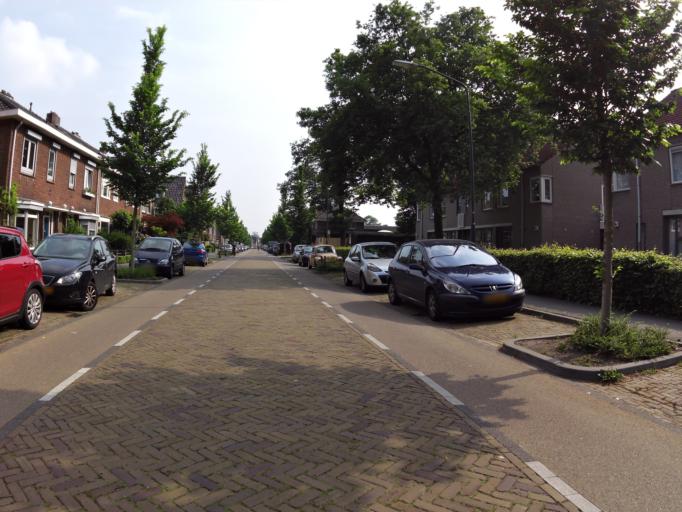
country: NL
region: North Brabant
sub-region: Gemeente Vught
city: Vught
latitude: 51.6518
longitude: 5.2830
